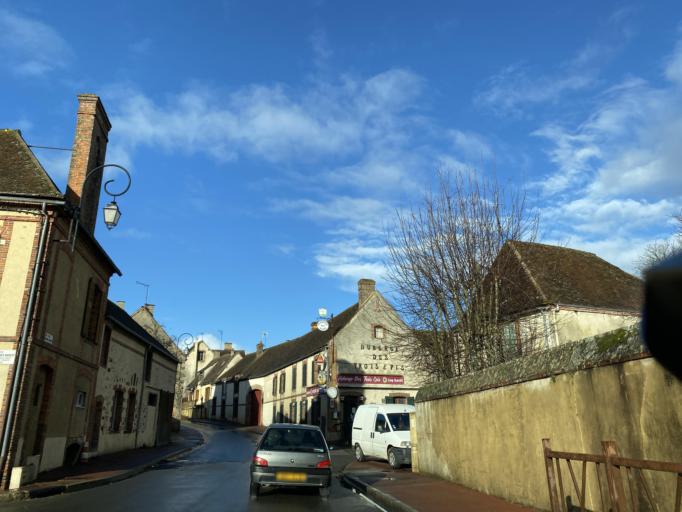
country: FR
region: Centre
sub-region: Departement d'Eure-et-Loir
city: Brezolles
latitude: 48.6310
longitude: 1.1484
